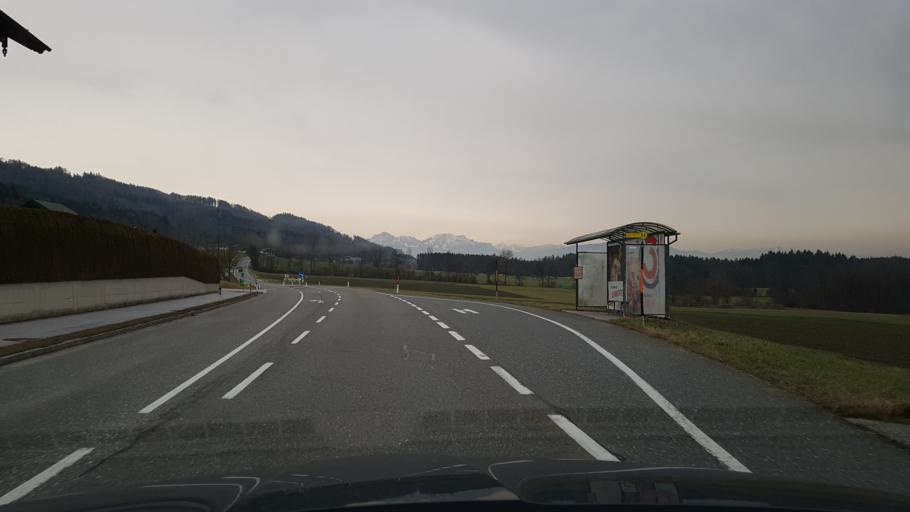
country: AT
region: Salzburg
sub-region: Politischer Bezirk Salzburg-Umgebung
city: Nussdorf am Haunsberg
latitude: 47.9492
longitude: 13.0025
